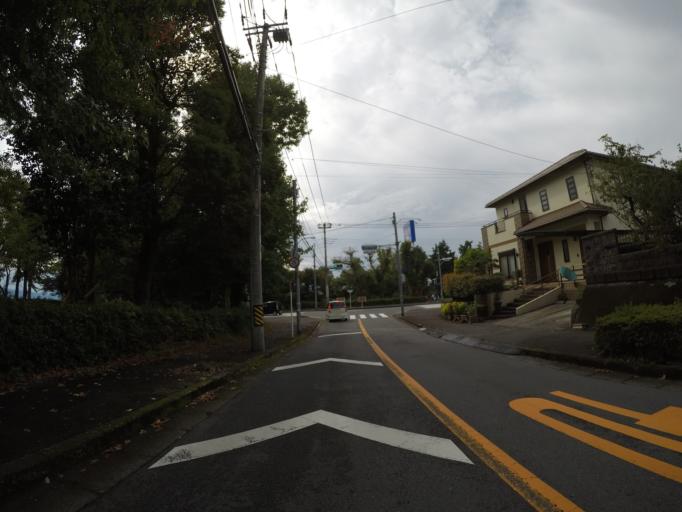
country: JP
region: Shizuoka
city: Fuji
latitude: 35.1783
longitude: 138.7186
